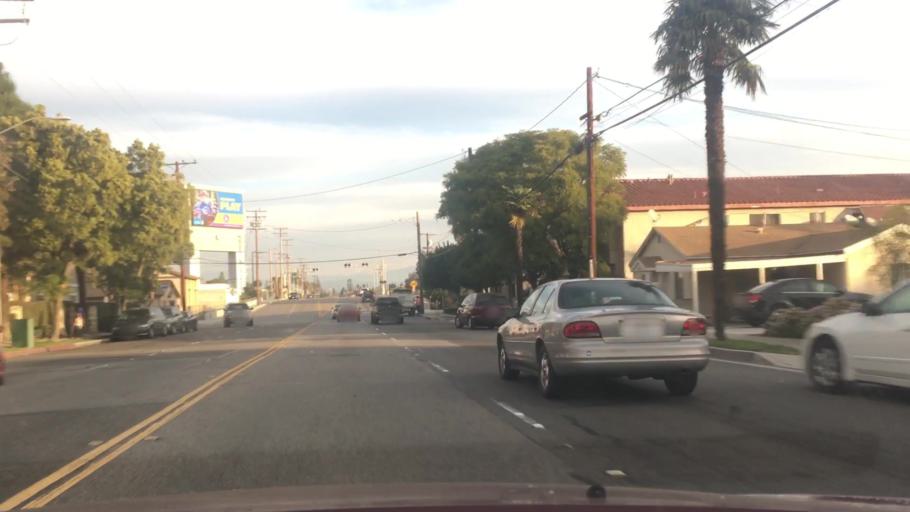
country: US
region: California
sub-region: Orange County
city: Buena Park
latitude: 33.8664
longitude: -118.0025
